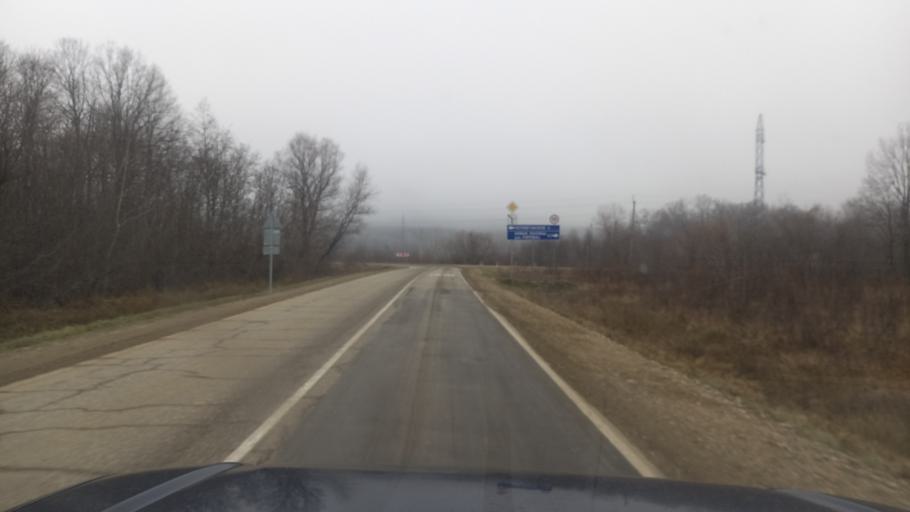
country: RU
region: Krasnodarskiy
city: Neftegorsk
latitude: 44.2891
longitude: 39.8162
